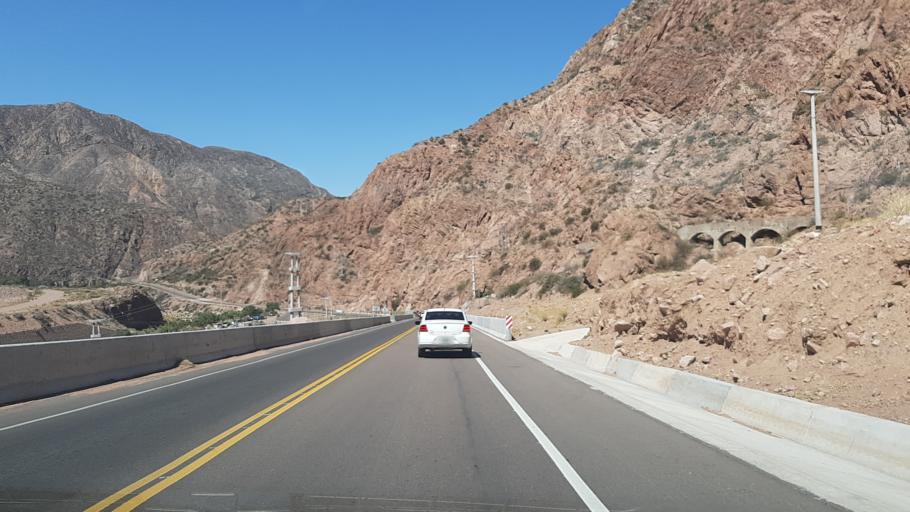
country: AR
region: Mendoza
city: Lujan de Cuyo
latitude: -33.0028
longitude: -69.1284
